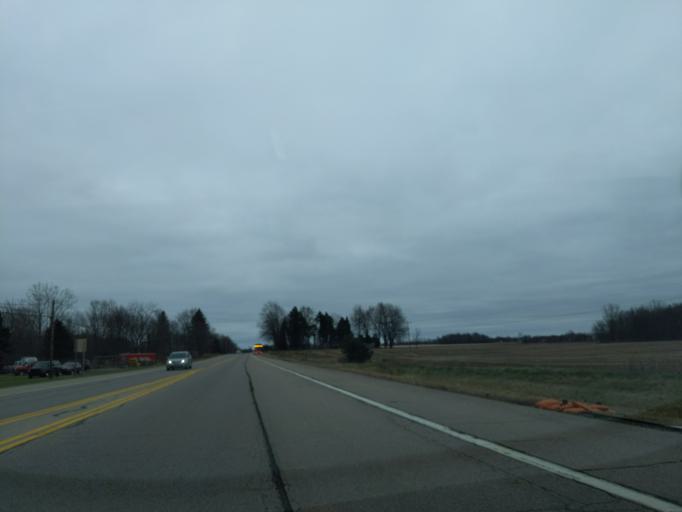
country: US
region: Michigan
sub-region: Clinton County
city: Saint Johns
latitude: 43.0013
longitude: -84.5132
